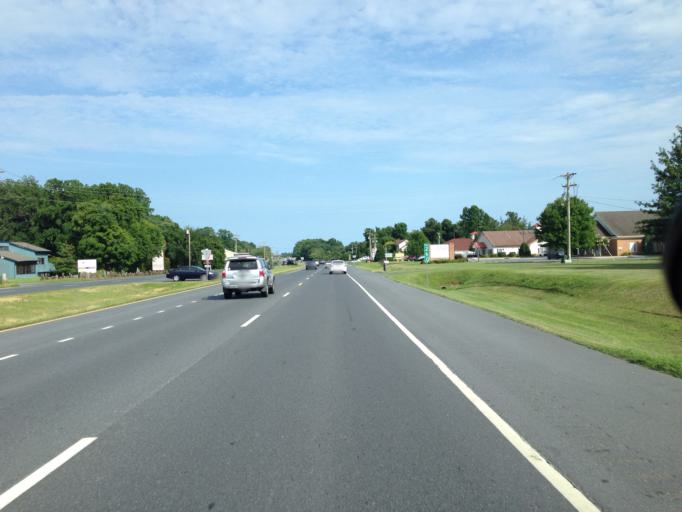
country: US
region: Delaware
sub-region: Sussex County
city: Lewes
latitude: 38.7636
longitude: -75.2086
